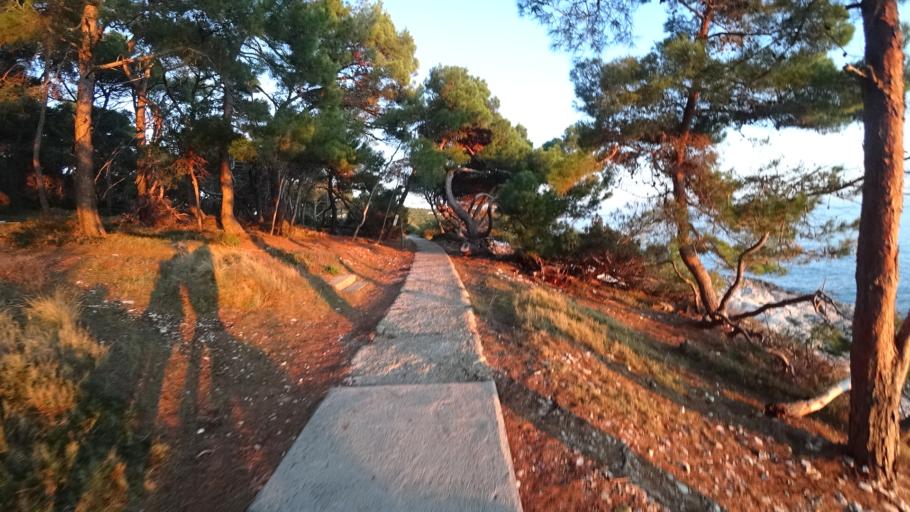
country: HR
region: Primorsko-Goranska
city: Mali Losinj
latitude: 44.5240
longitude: 14.4509
